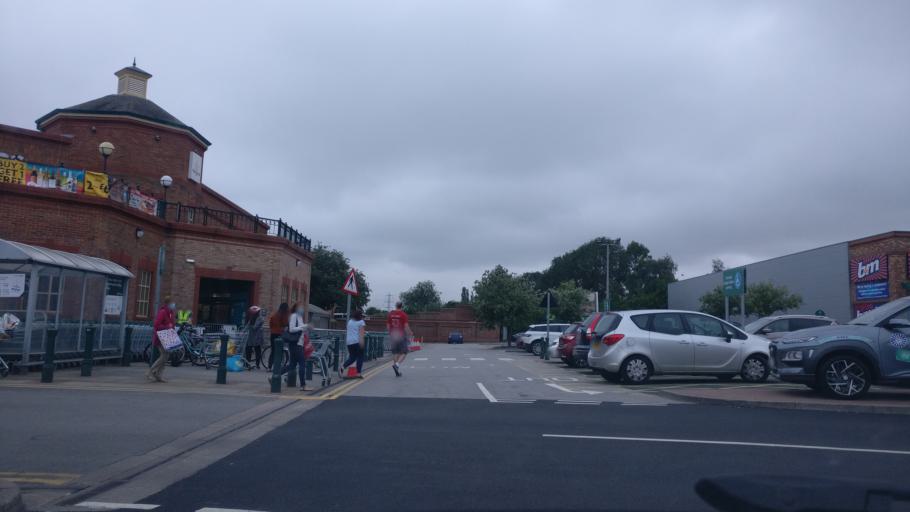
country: GB
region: England
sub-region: East Riding of Yorkshire
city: Beverley
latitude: 53.8235
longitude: -0.4423
